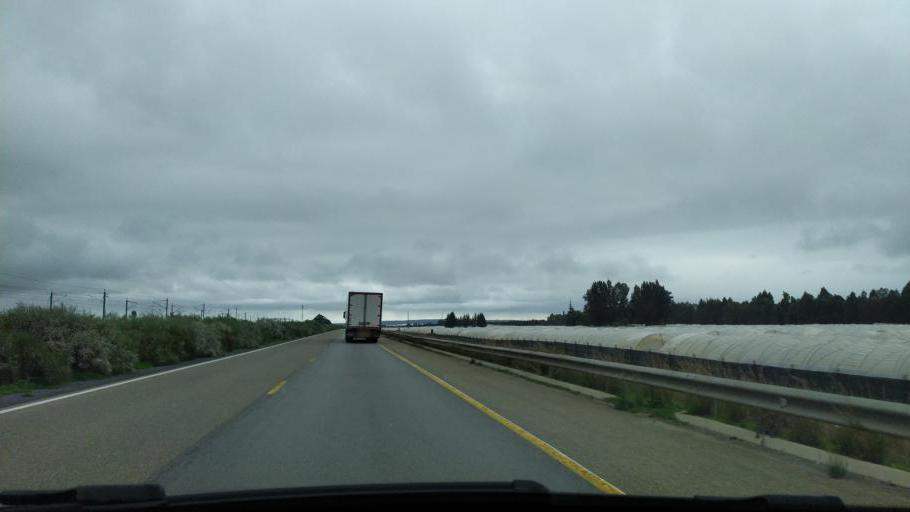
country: MA
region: Gharb-Chrarda-Beni Hssen
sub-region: Kenitra Province
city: Lalla Mimouna
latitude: 34.8996
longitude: -6.2092
